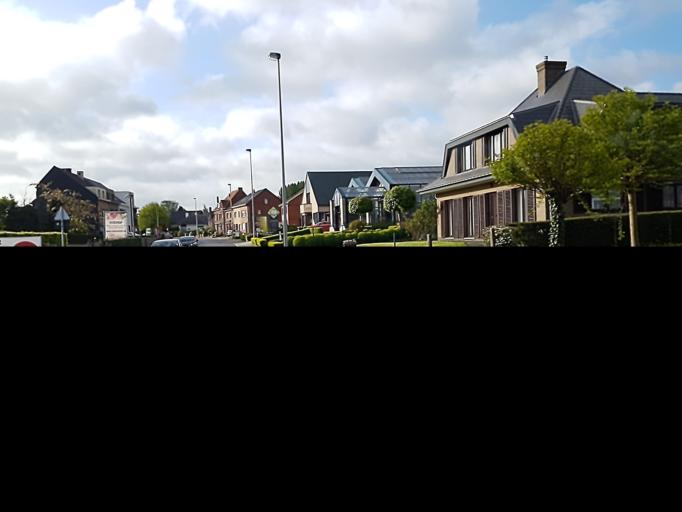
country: BE
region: Flanders
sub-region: Provincie Oost-Vlaanderen
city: Temse
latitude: 51.1312
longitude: 4.1934
